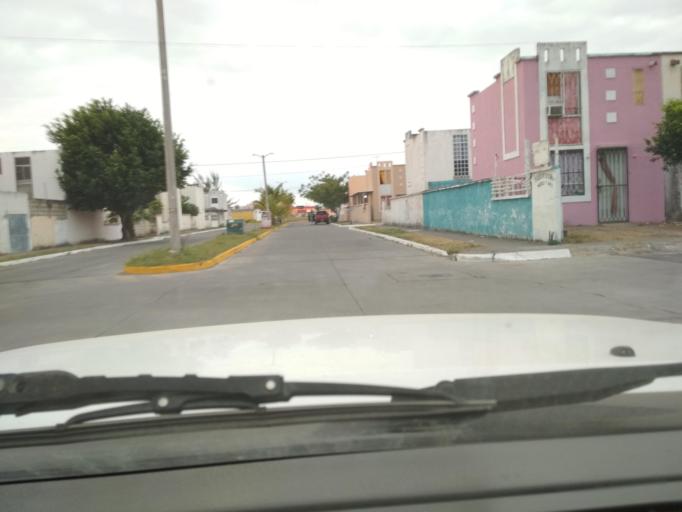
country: MX
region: Veracruz
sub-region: Medellin
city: Fraccionamiento Arboledas San Ramon
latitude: 19.0943
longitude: -96.1604
